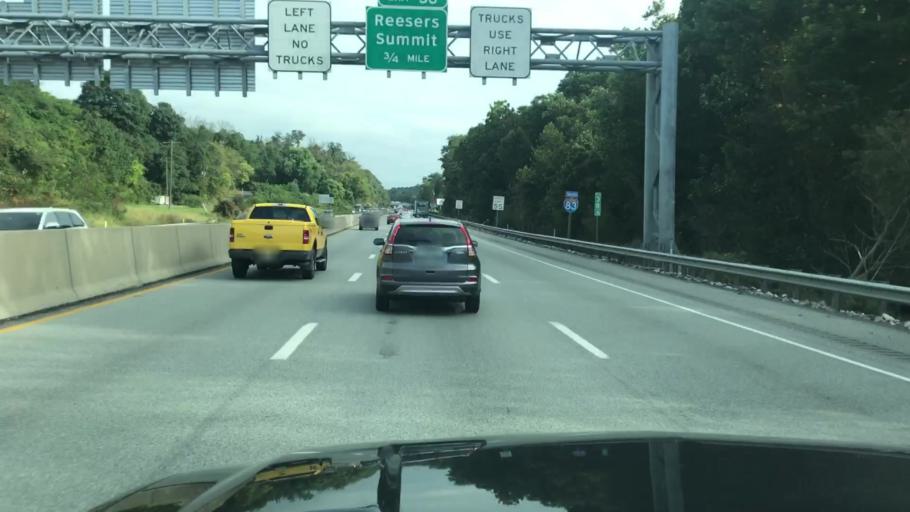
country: US
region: Pennsylvania
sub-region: Cumberland County
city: New Cumberland
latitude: 40.2048
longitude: -76.8728
